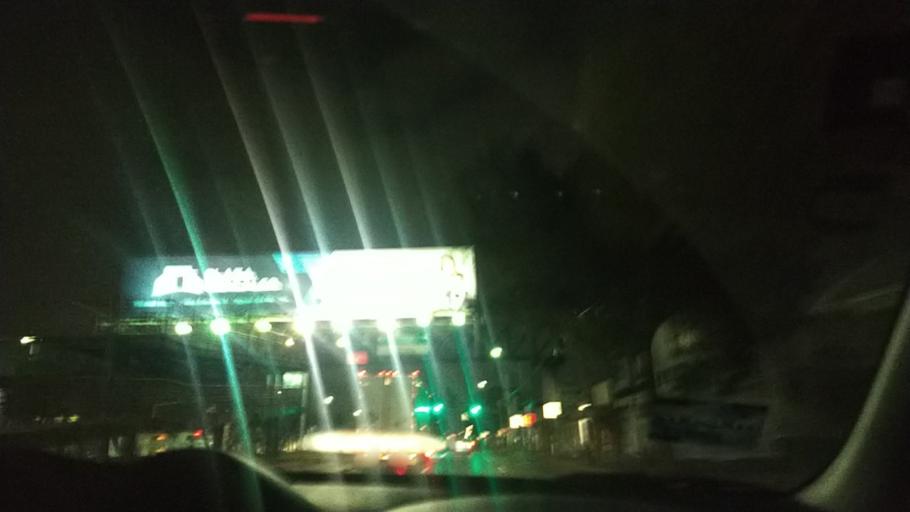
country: MX
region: Mexico
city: Ecatepec
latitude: 19.6220
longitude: -99.0723
